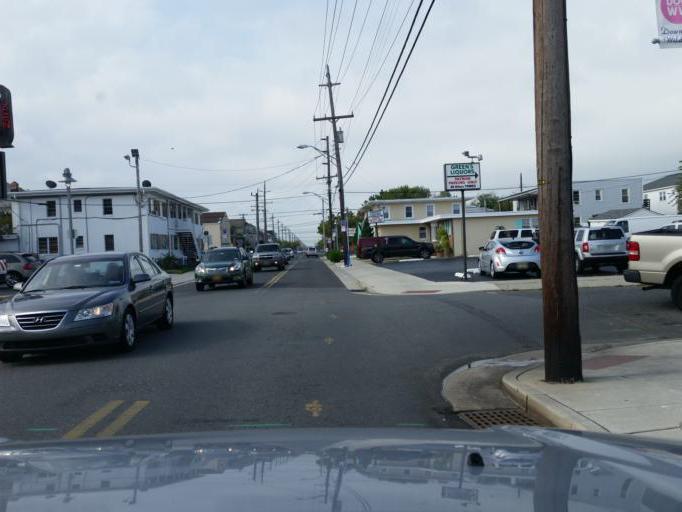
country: US
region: New Jersey
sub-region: Cape May County
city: Wildwood Crest
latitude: 38.9808
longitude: -74.8255
